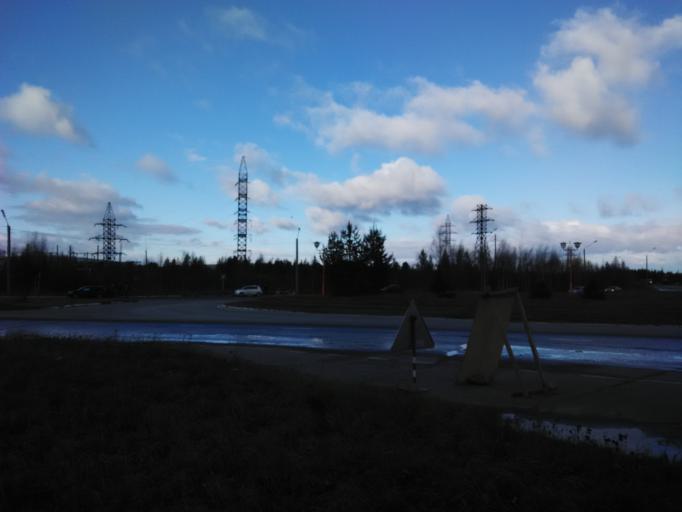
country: RU
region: Murmansk
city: Polyarnyye Zori
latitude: 67.3722
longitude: 32.5043
